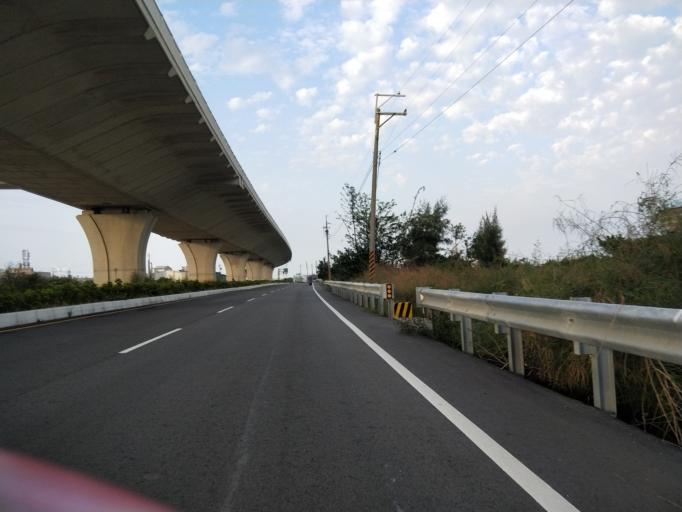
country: TW
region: Taiwan
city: Fengyuan
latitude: 24.4127
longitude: 120.6164
